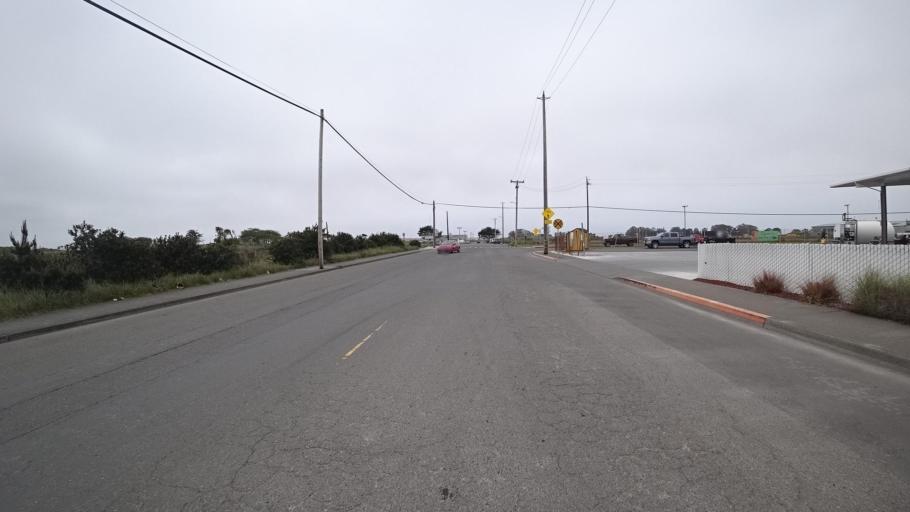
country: US
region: California
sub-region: Humboldt County
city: Bayview
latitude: 40.7908
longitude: -124.1843
